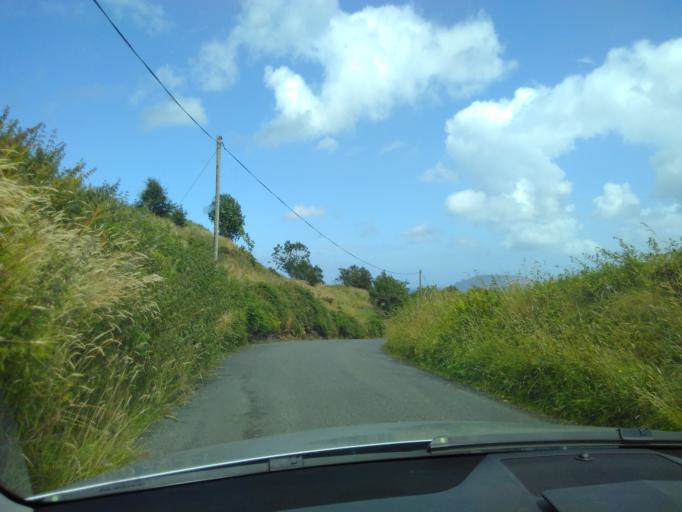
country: IE
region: Ulster
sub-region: County Donegal
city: Ramelton
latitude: 55.2275
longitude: -7.6218
